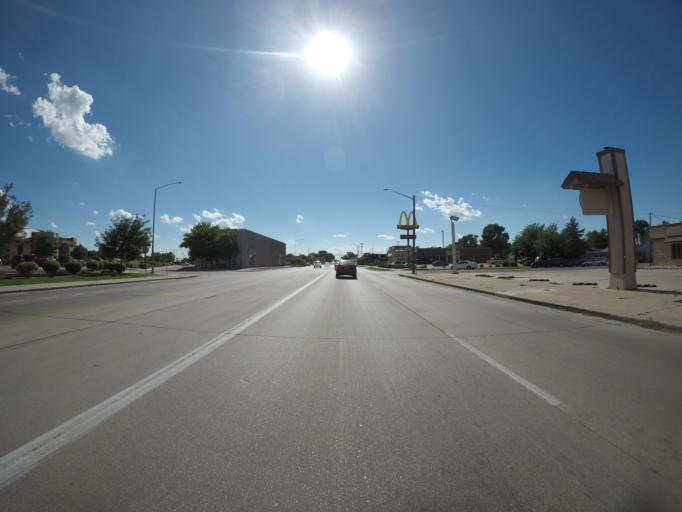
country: US
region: Colorado
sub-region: Logan County
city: Sterling
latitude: 40.6255
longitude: -103.2128
